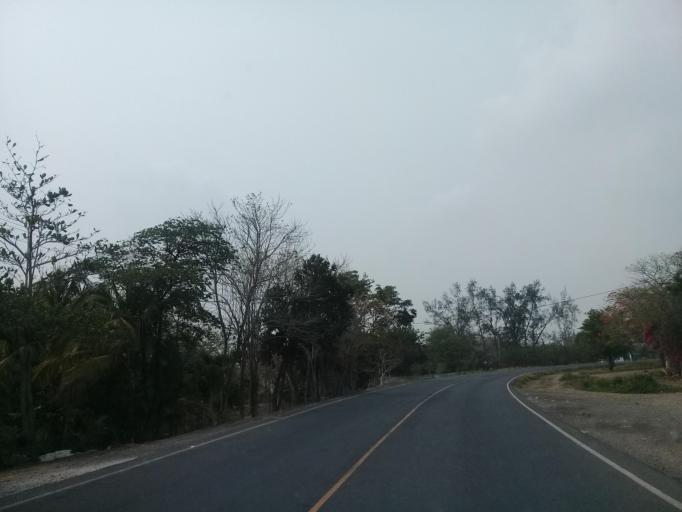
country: MX
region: Veracruz
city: Jamapa
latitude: 18.9187
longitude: -96.1968
